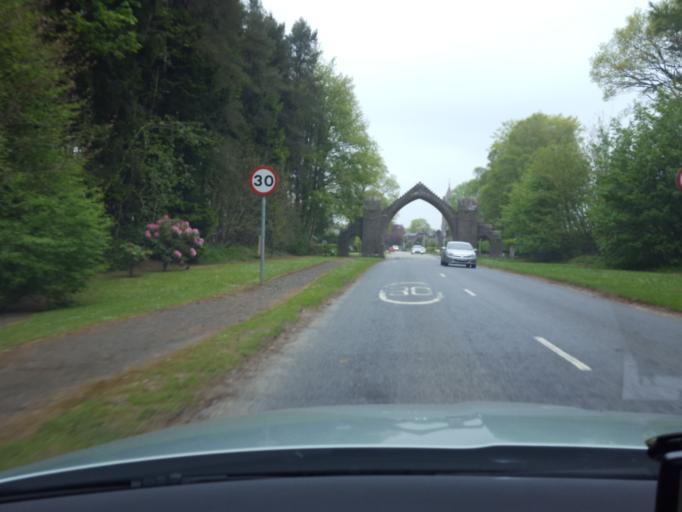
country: GB
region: Scotland
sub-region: Angus
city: Brechin
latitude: 56.8049
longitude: -2.6531
